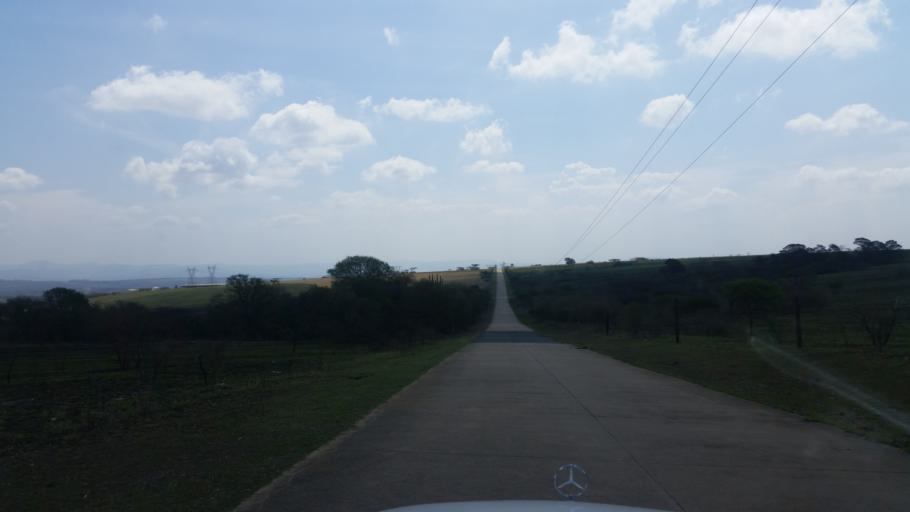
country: ZA
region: KwaZulu-Natal
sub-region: uMgungundlovu District Municipality
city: Camperdown
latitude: -29.6726
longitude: 30.5141
